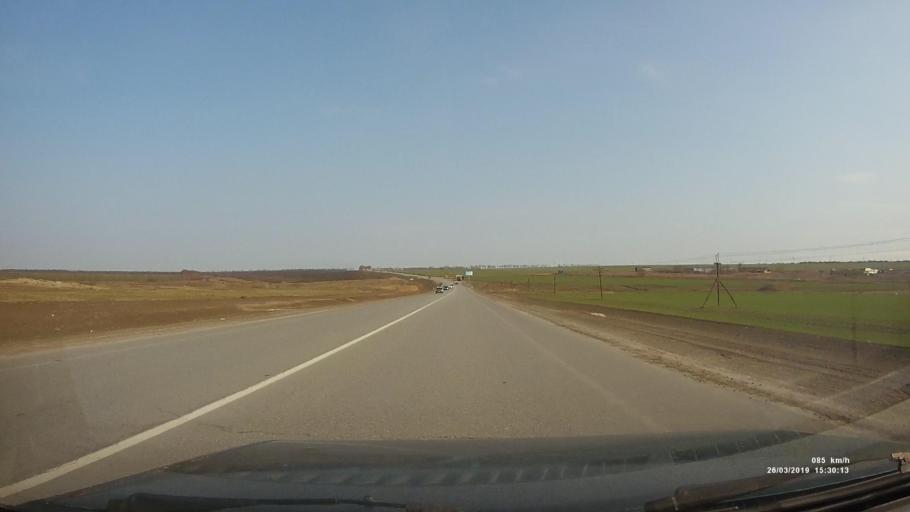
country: RU
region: Rostov
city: Primorka
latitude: 47.3112
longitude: 39.1128
